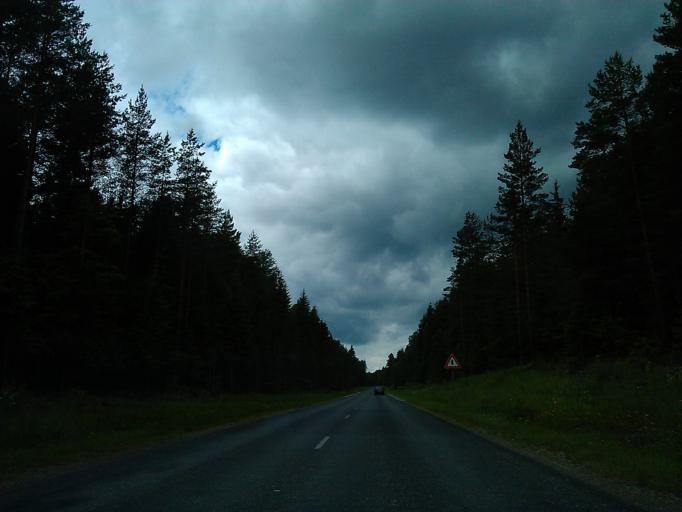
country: LV
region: Talsu Rajons
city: Stende
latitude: 57.0892
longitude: 22.4021
